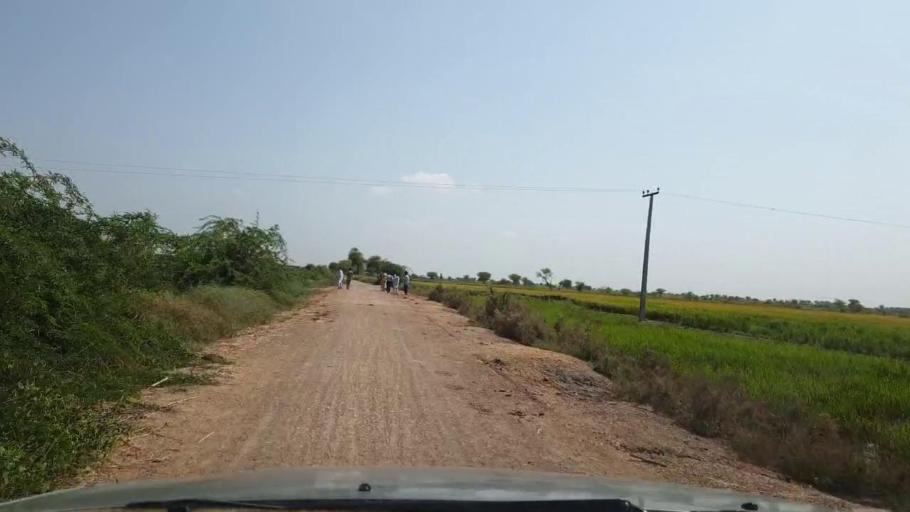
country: PK
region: Sindh
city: Rajo Khanani
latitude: 25.0218
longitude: 68.7980
